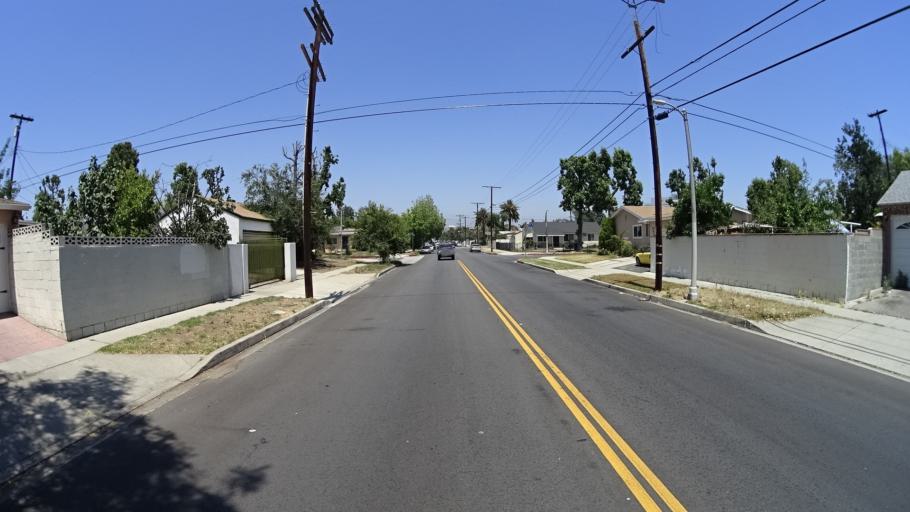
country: US
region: California
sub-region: Los Angeles County
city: Van Nuys
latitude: 34.2181
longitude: -118.4340
